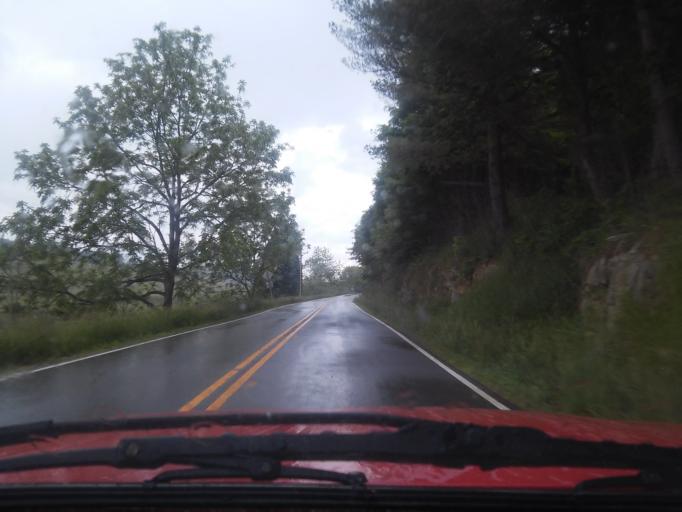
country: US
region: Virginia
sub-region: Montgomery County
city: Blacksburg
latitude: 37.3973
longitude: -80.3163
